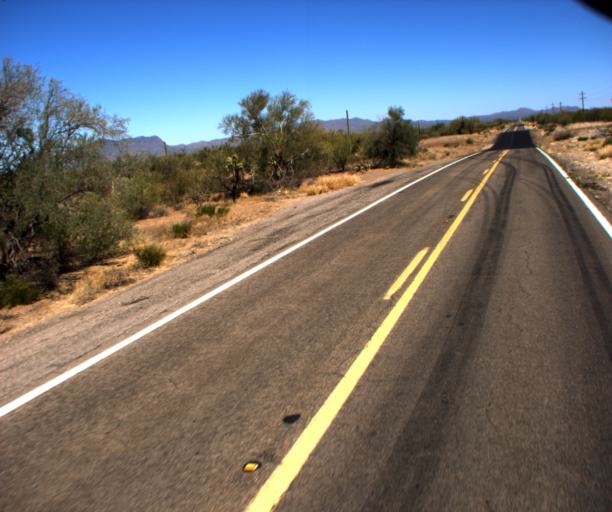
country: US
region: Arizona
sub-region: Pima County
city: Sells
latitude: 32.0231
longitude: -112.0037
